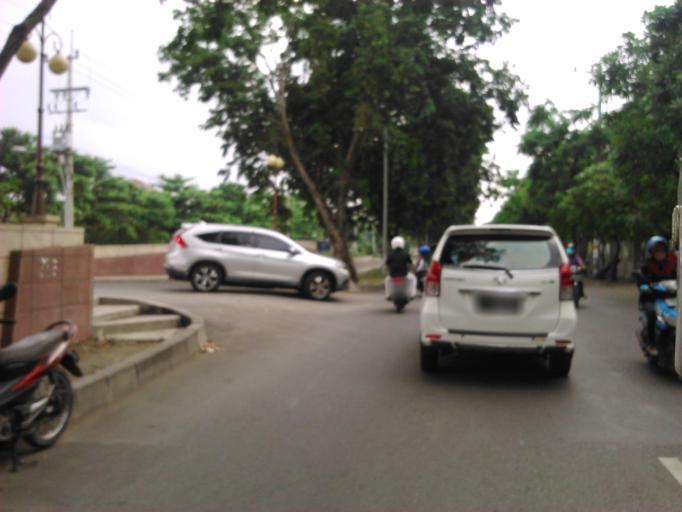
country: ID
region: East Java
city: Semampir
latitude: -7.2906
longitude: 112.7910
